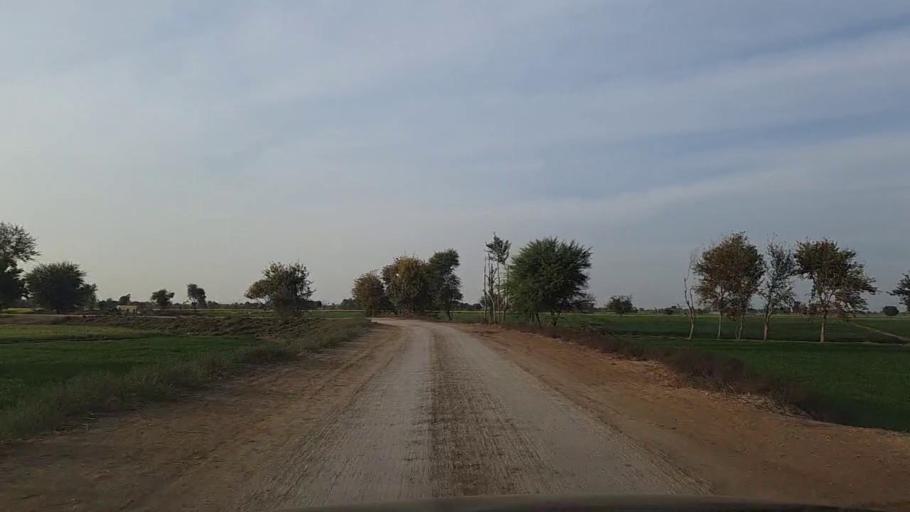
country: PK
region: Sindh
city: Jam Sahib
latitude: 26.4343
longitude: 68.5640
